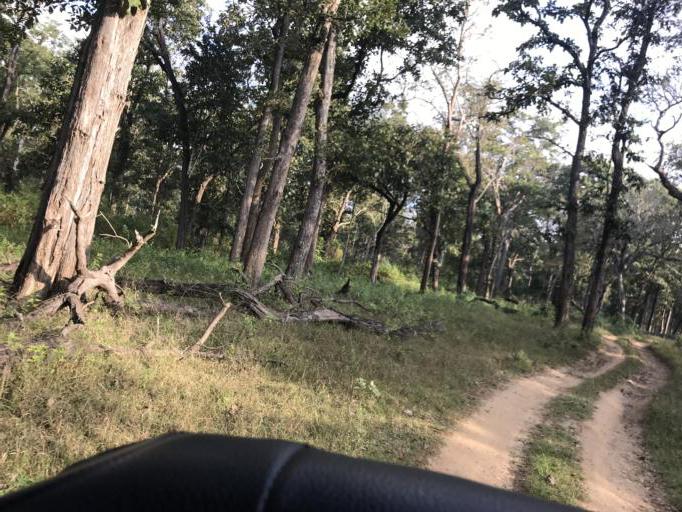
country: IN
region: Karnataka
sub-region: Mysore
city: Heggadadevankote
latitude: 11.9617
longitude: 76.2018
